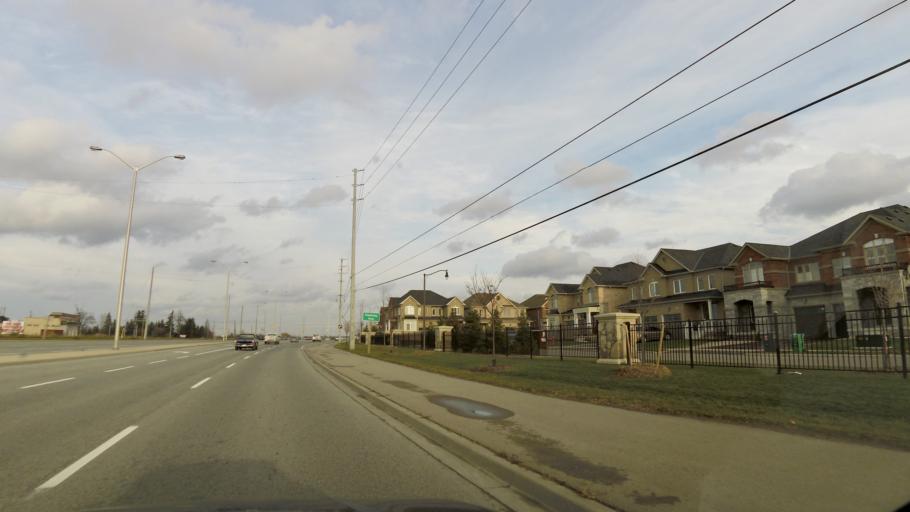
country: CA
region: Ontario
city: Brampton
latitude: 43.7996
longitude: -79.6809
